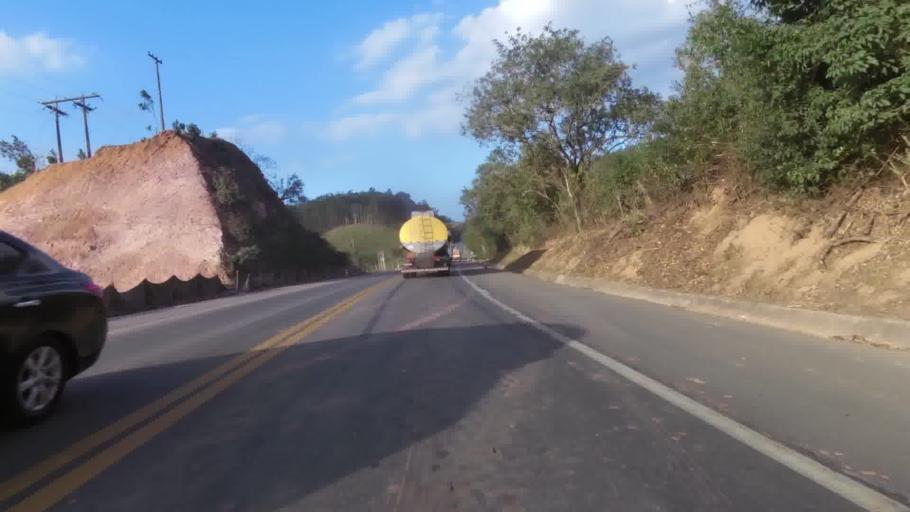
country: BR
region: Espirito Santo
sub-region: Rio Novo Do Sul
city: Rio Novo do Sul
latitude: -20.8961
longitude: -41.0085
